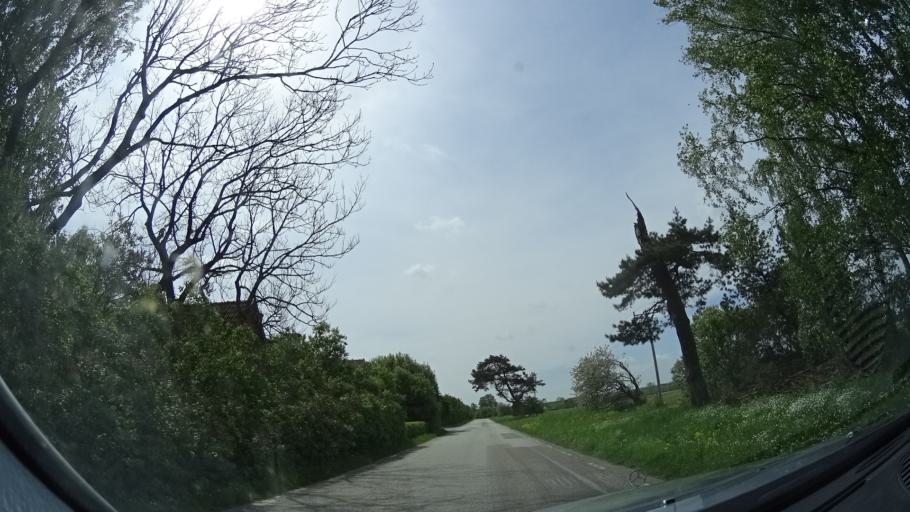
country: SE
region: Skane
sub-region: Sjobo Kommun
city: Sjoebo
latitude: 55.6750
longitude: 13.6249
